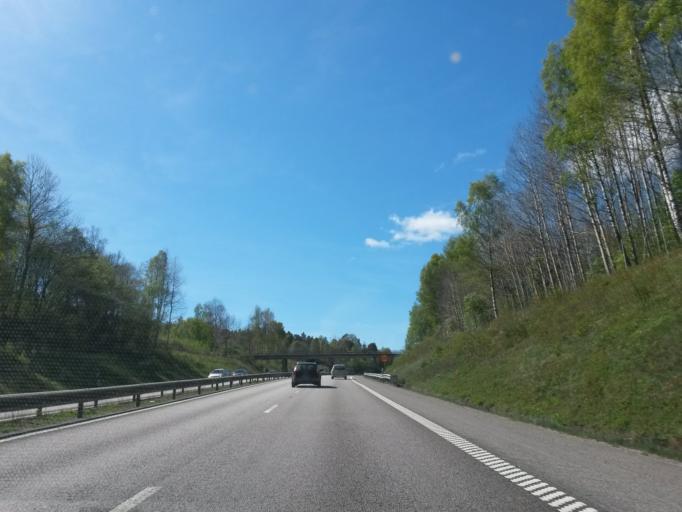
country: SE
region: Vaestra Goetaland
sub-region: Lerums Kommun
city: Lerum
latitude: 57.7494
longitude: 12.2373
